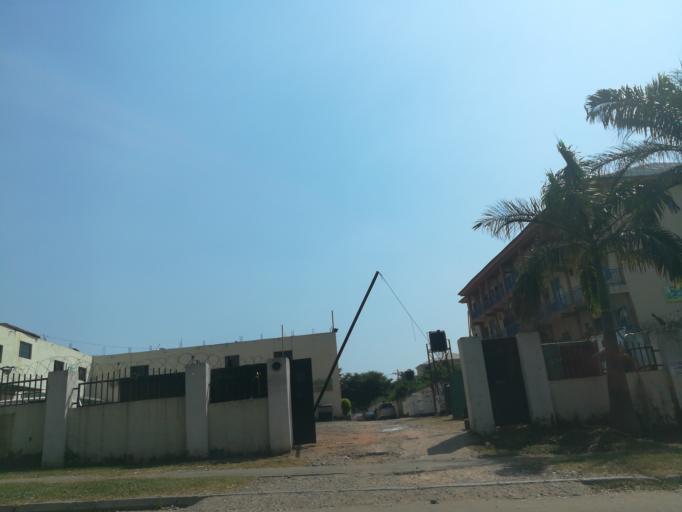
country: NG
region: Abuja Federal Capital Territory
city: Abuja
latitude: 9.0683
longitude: 7.4385
